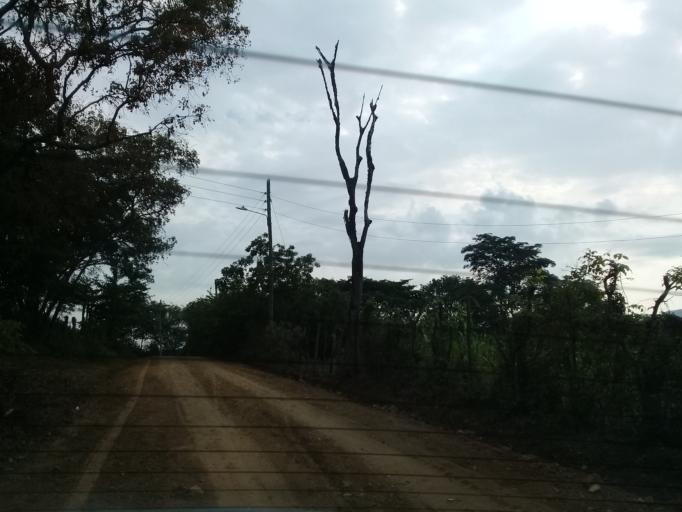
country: CO
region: Cundinamarca
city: Ricaurte
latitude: 4.3467
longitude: -74.7383
